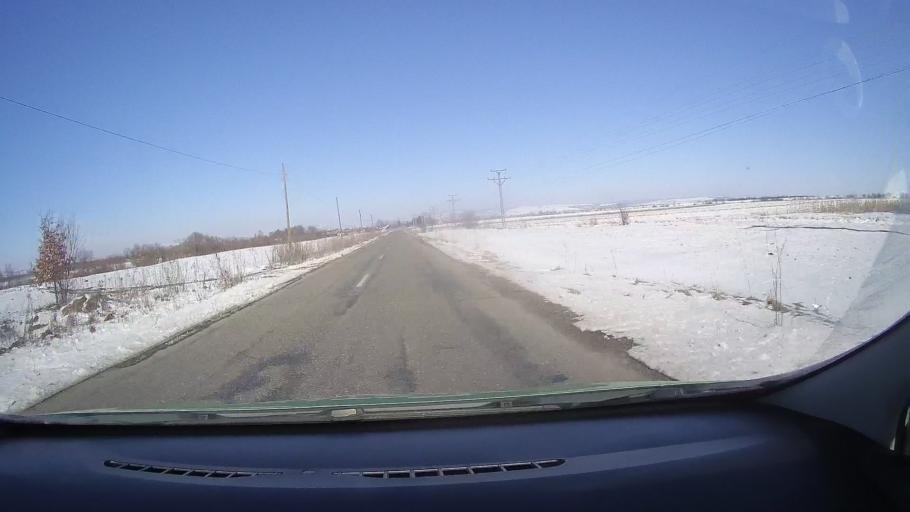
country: RO
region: Brasov
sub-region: Comuna Harseni
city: Harseni
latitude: 45.7756
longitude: 25.0011
